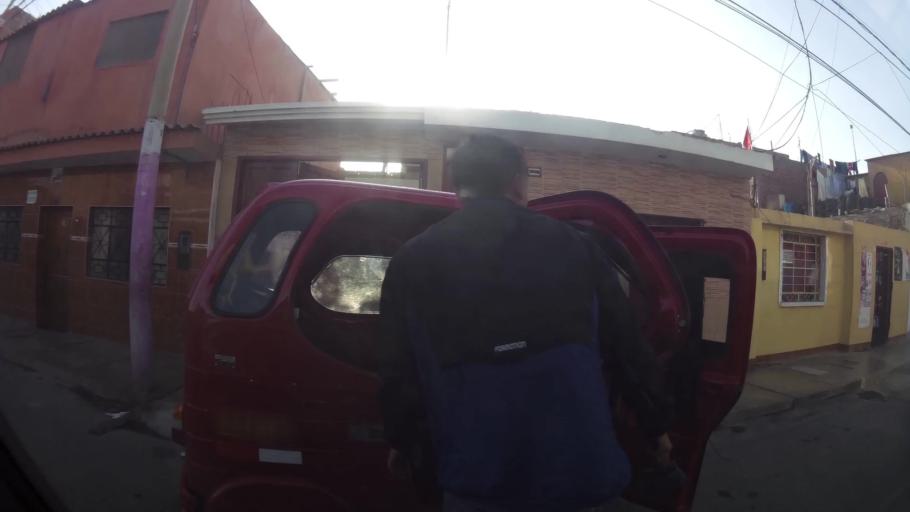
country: PE
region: Lima
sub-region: Huaura
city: Huacho
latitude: -11.1132
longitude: -77.6061
